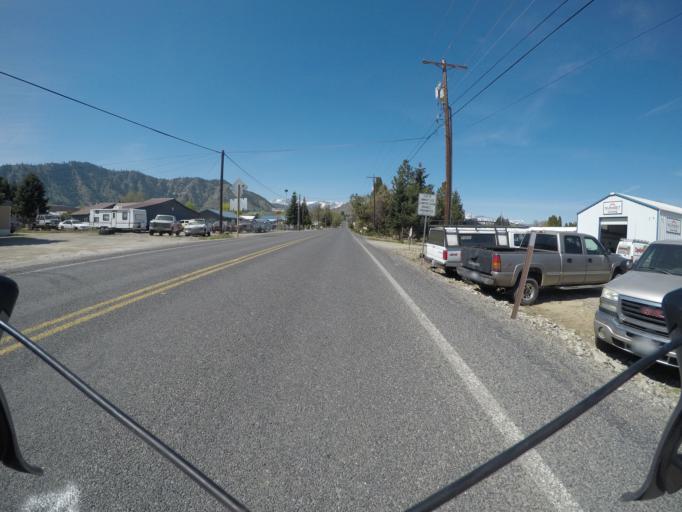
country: US
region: Washington
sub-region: Chelan County
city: Cashmere
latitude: 47.5246
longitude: -120.4880
